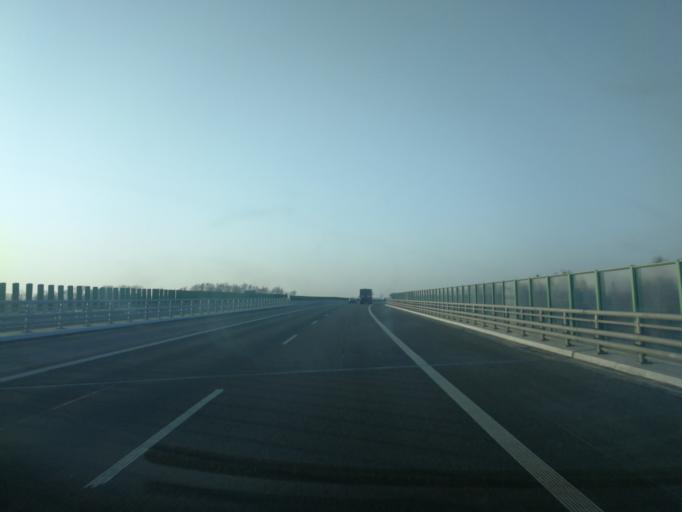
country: PL
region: Pomeranian Voivodeship
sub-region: Powiat nowodworski
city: Nowy Dwor Gdanski
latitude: 54.1999
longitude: 19.1175
